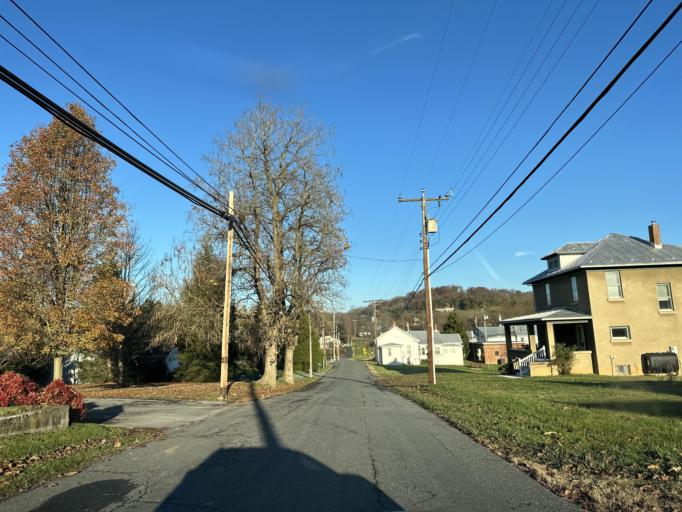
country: US
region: Virginia
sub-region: Augusta County
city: Weyers Cave
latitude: 38.2874
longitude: -78.9127
